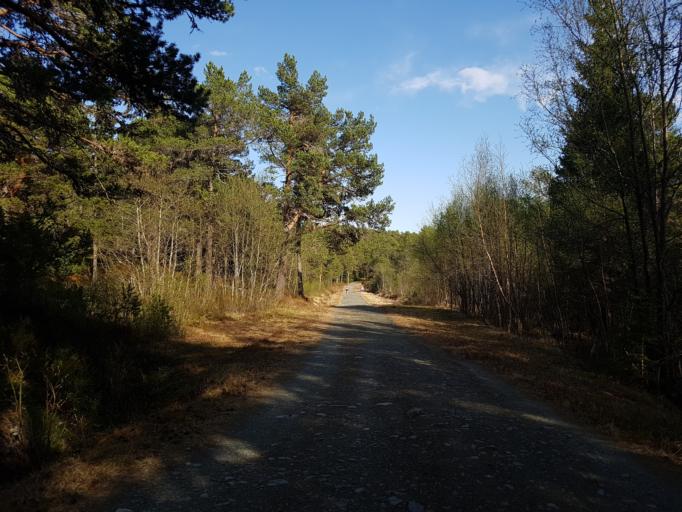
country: NO
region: Sor-Trondelag
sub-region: Trondheim
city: Trondheim
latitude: 63.4412
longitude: 10.3174
